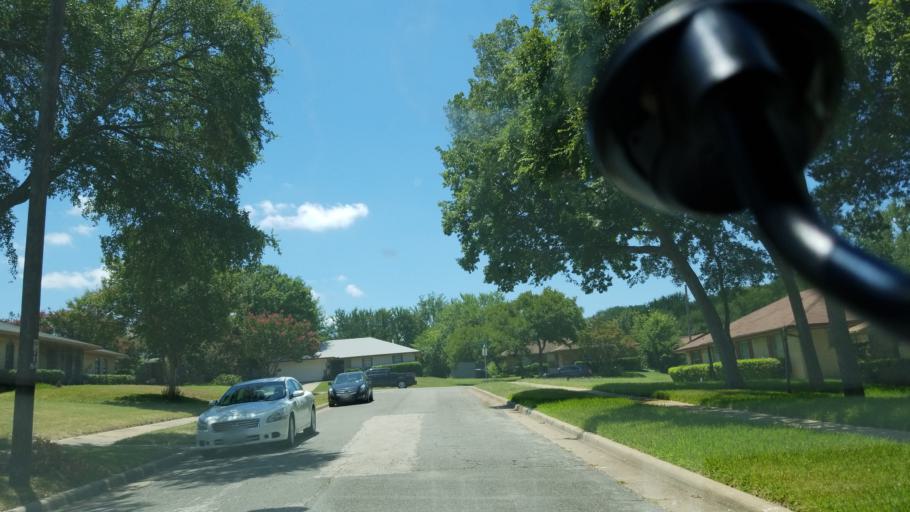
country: US
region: Texas
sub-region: Dallas County
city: Cockrell Hill
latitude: 32.6785
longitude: -96.8160
